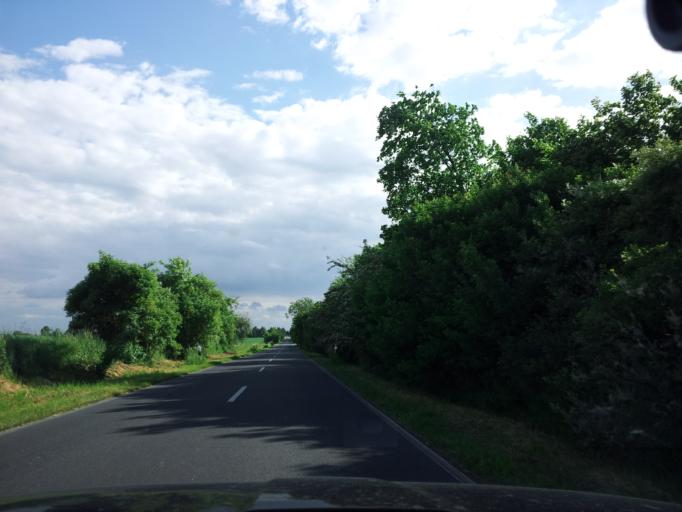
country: DE
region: Saxony-Anhalt
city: Seyda
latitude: 51.9649
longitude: 12.9014
